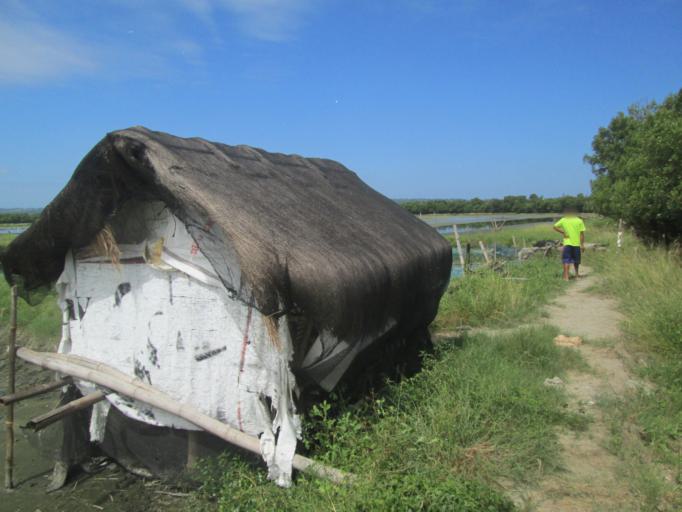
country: PH
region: Ilocos
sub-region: Province of Pangasinan
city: Pangapisan
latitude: 16.2452
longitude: 119.9287
